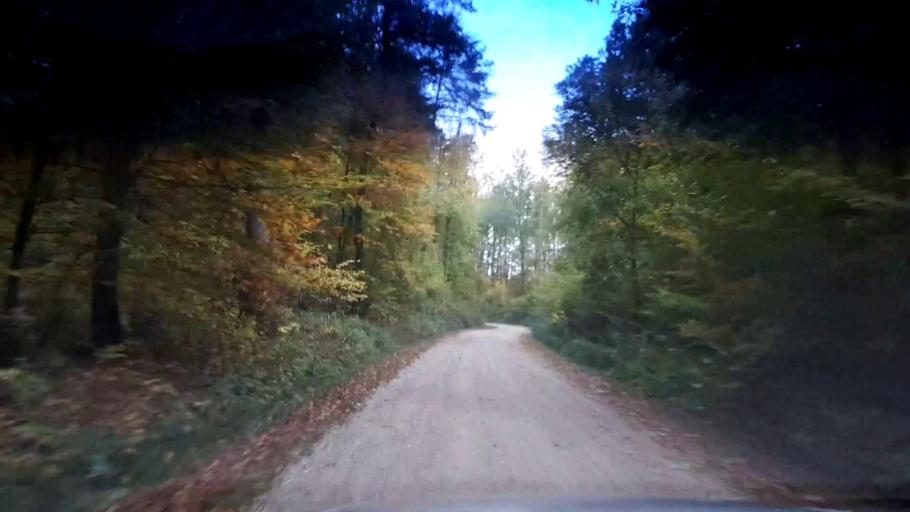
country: DE
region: Bavaria
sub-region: Upper Franconia
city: Schesslitz
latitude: 49.9617
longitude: 11.0313
